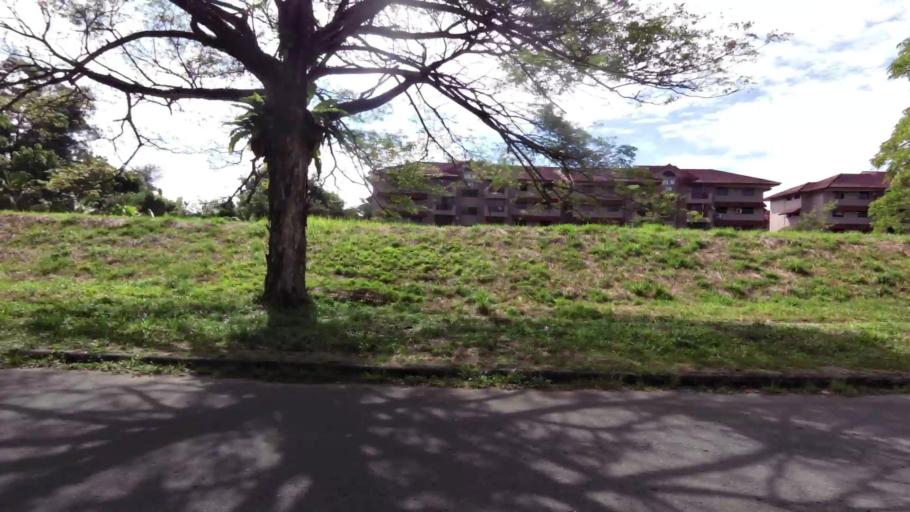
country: BN
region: Brunei and Muara
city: Bandar Seri Begawan
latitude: 4.9352
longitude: 114.9068
